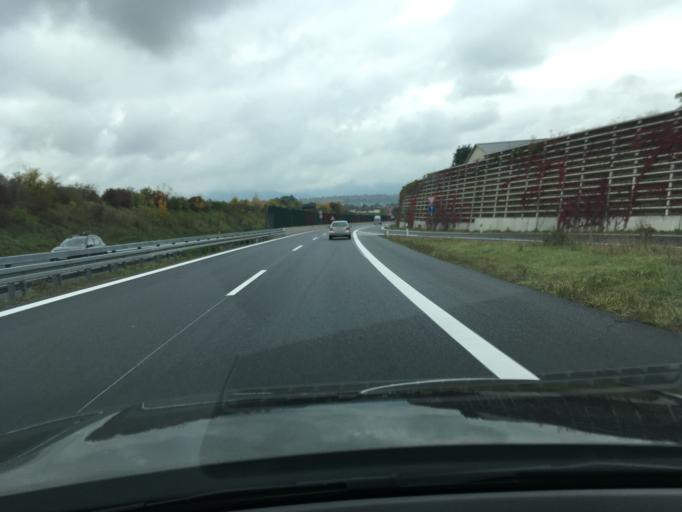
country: DE
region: Baden-Wuerttemberg
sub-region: Tuebingen Region
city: Dusslingen
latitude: 48.4559
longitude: 9.0621
